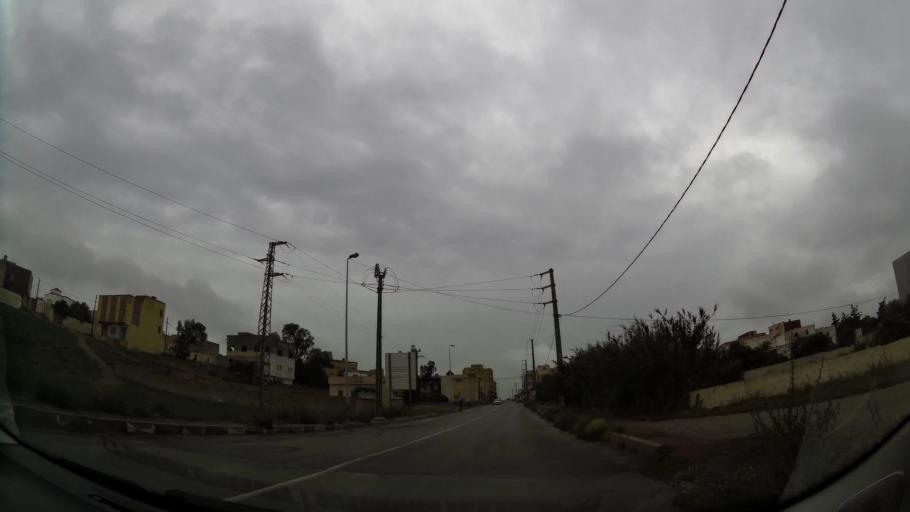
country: MA
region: Oriental
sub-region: Nador
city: Nador
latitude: 35.1529
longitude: -3.0253
